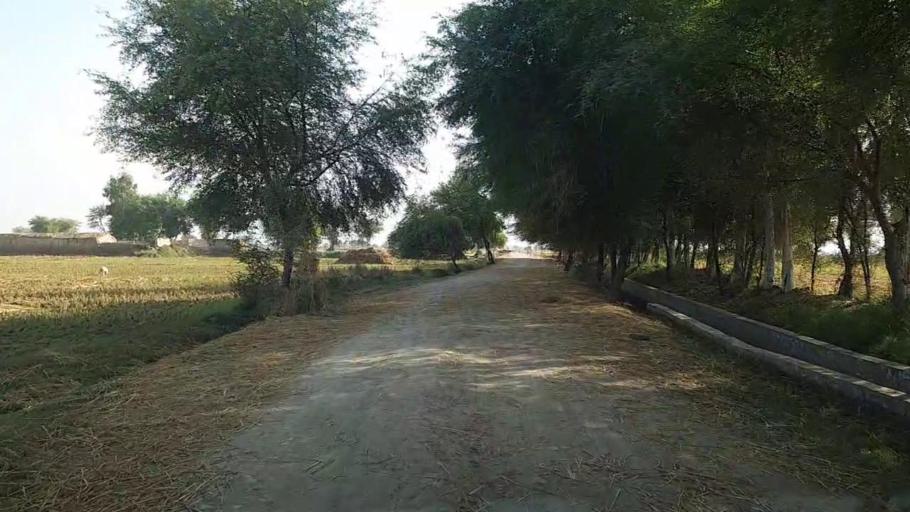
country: PK
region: Sindh
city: Kandhkot
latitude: 28.3521
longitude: 69.3352
